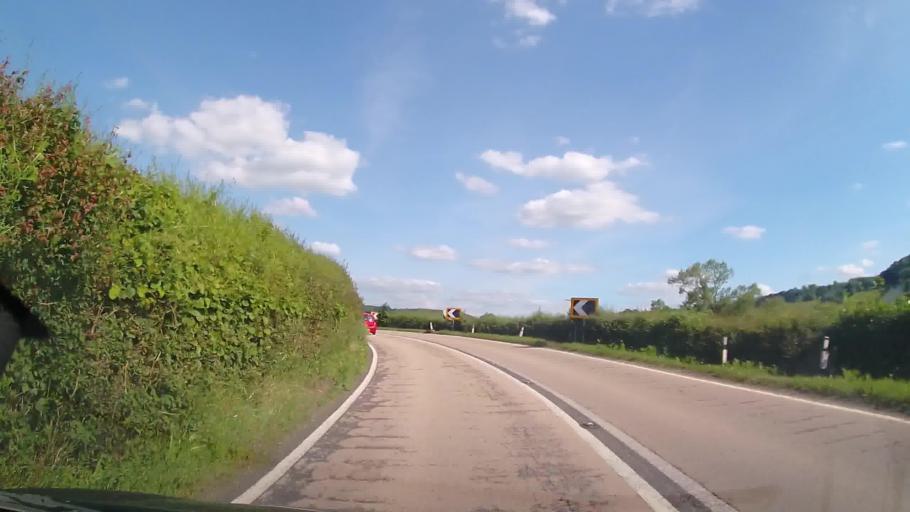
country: GB
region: Wales
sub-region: Sir Powys
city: Welshpool
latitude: 52.6509
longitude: -3.2510
